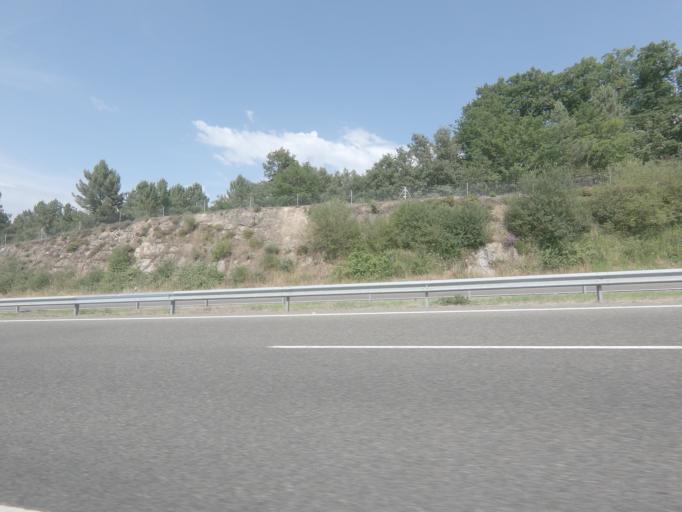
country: ES
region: Galicia
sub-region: Provincia de Ourense
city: Taboadela
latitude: 42.2731
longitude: -7.8721
